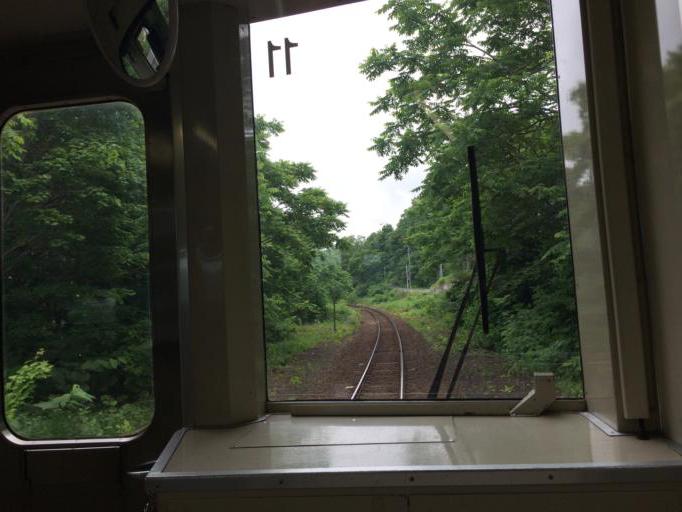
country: JP
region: Hokkaido
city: Otaru
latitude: 43.2110
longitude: 140.9633
